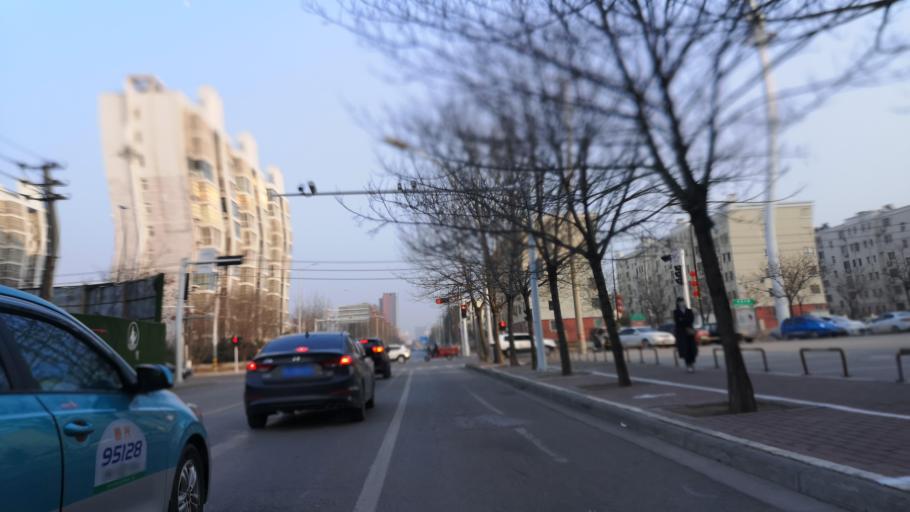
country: CN
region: Henan Sheng
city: Zhongyuanlu
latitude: 35.7641
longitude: 115.0566
